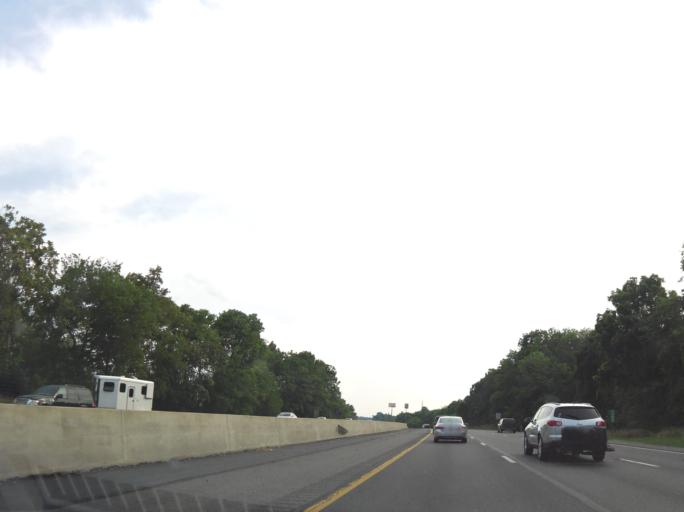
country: US
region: West Virginia
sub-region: Berkeley County
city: Martinsburg
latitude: 39.4906
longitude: -77.9716
